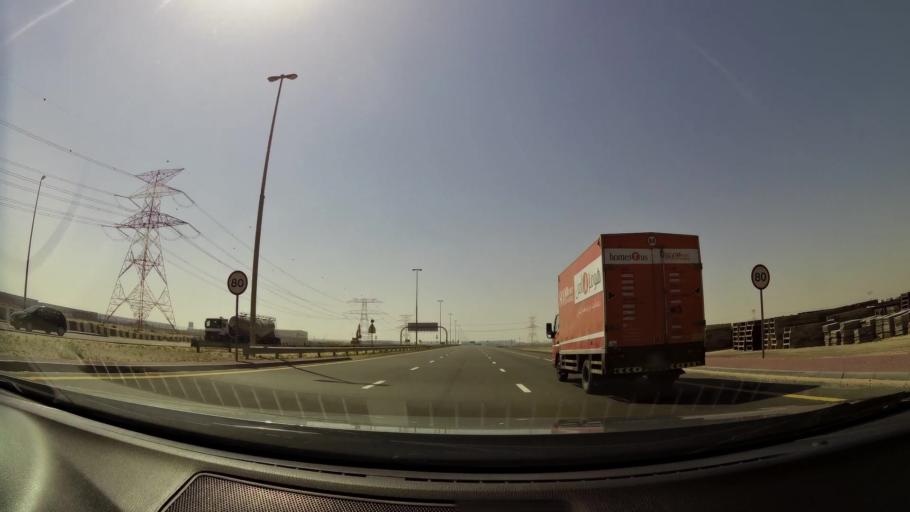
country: AE
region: Dubai
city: Dubai
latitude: 24.9265
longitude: 55.0928
